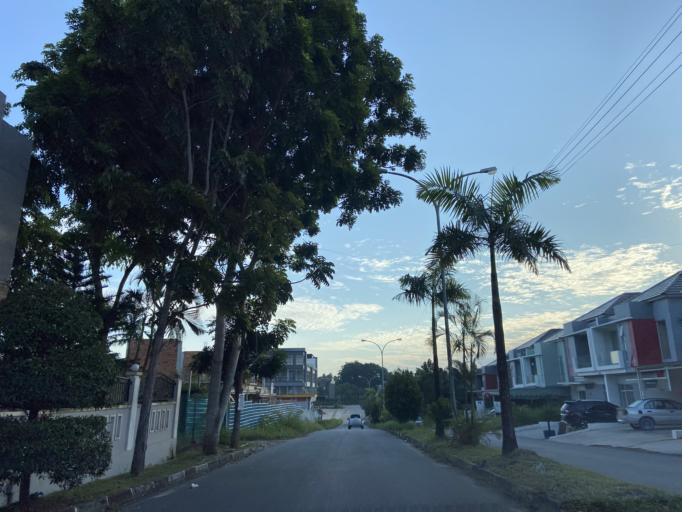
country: SG
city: Singapore
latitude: 1.1236
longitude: 104.0412
